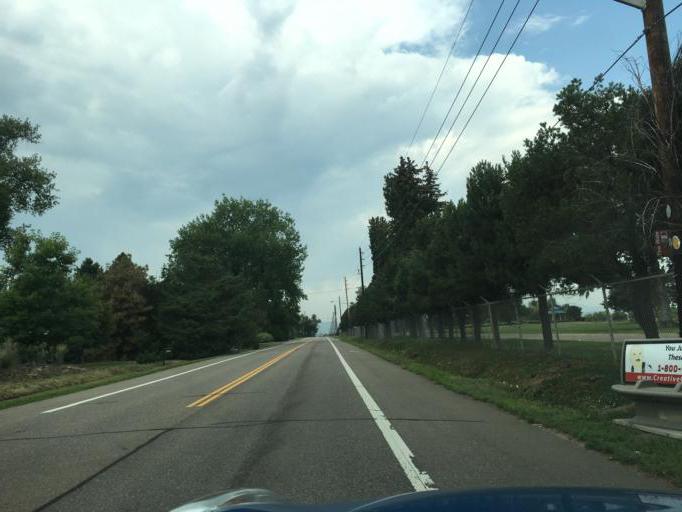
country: US
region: Colorado
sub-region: Jefferson County
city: Wheat Ridge
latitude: 39.7548
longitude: -105.0972
